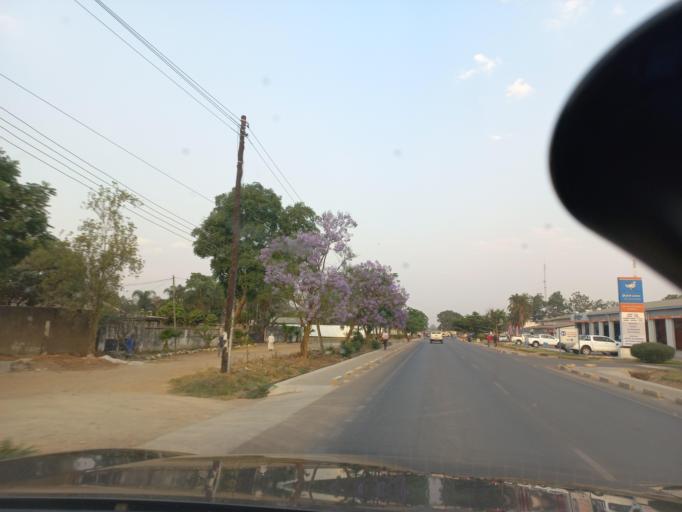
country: ZM
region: Lusaka
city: Lusaka
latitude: -15.3945
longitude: 28.2771
